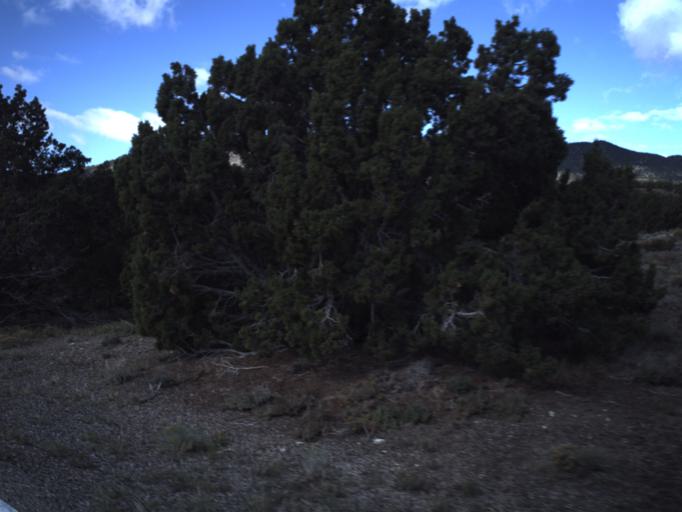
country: US
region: Utah
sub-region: Beaver County
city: Milford
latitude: 38.4607
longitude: -113.2514
